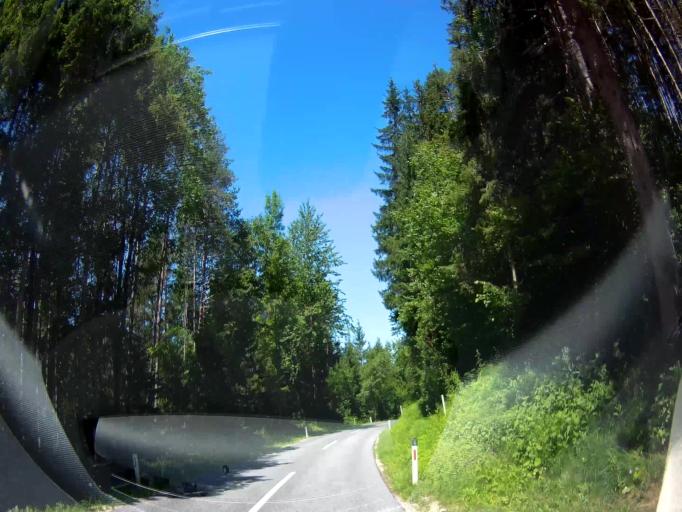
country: AT
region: Carinthia
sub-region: Politischer Bezirk Klagenfurt Land
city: Ferlach
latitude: 46.5138
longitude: 14.2935
